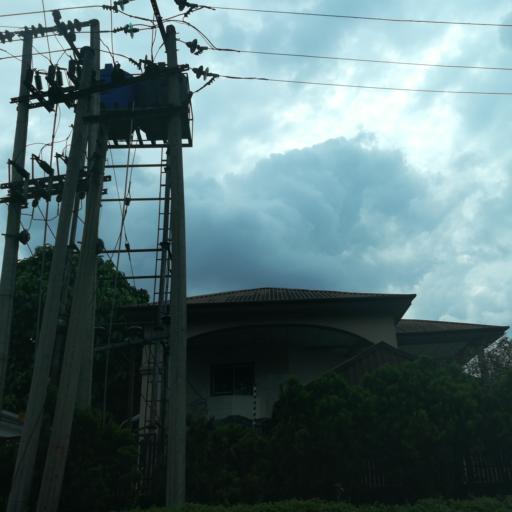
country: NG
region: Rivers
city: Port Harcourt
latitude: 4.8288
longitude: 6.9959
